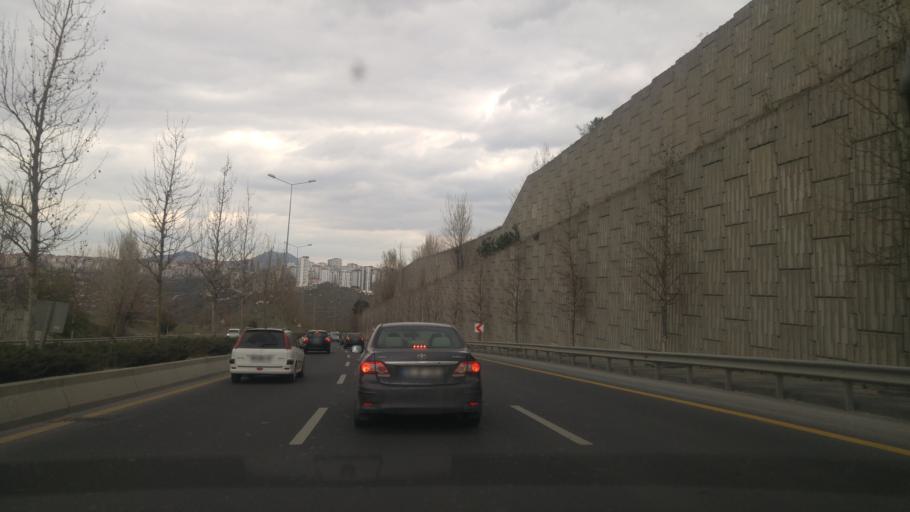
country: TR
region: Ankara
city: Cankaya
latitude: 39.8879
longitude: 32.8962
